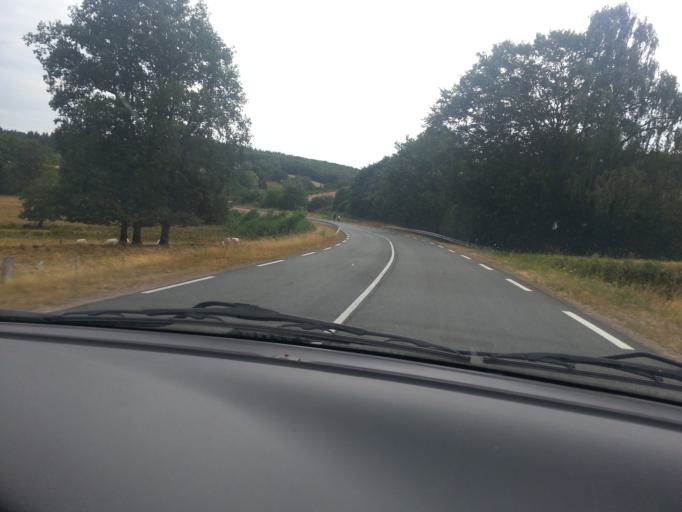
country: FR
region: Auvergne
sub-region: Departement de l'Allier
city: Lapalisse
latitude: 46.2634
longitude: 3.7277
